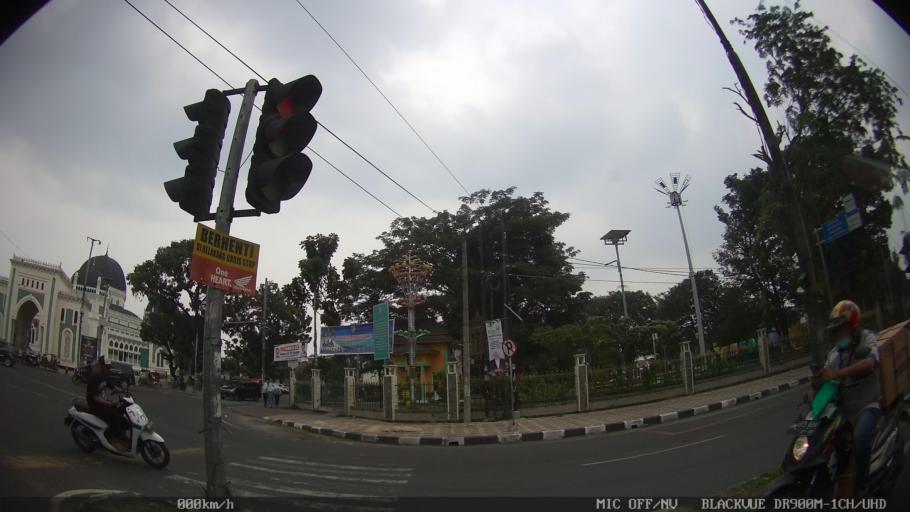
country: ID
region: North Sumatra
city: Medan
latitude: 3.5762
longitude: 98.6875
